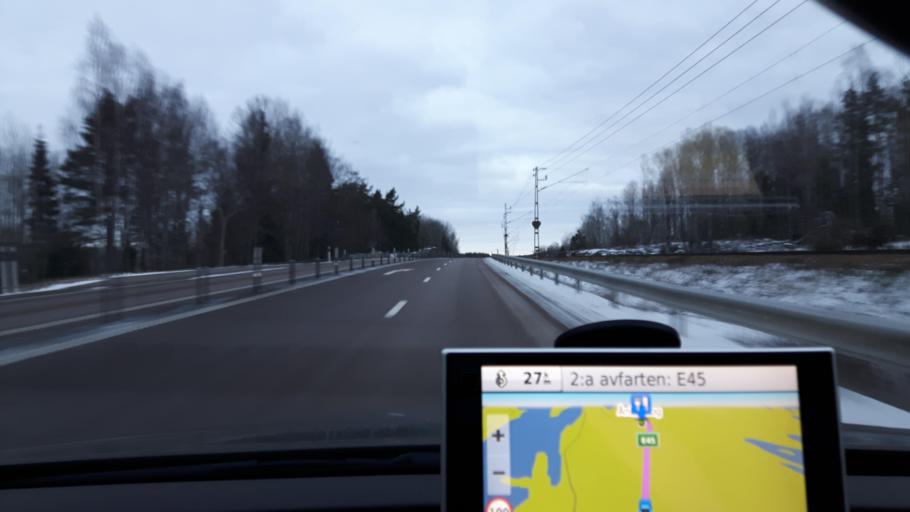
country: SE
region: Vaestra Goetaland
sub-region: Melleruds Kommun
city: Mellerud
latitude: 58.8476
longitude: 12.5515
